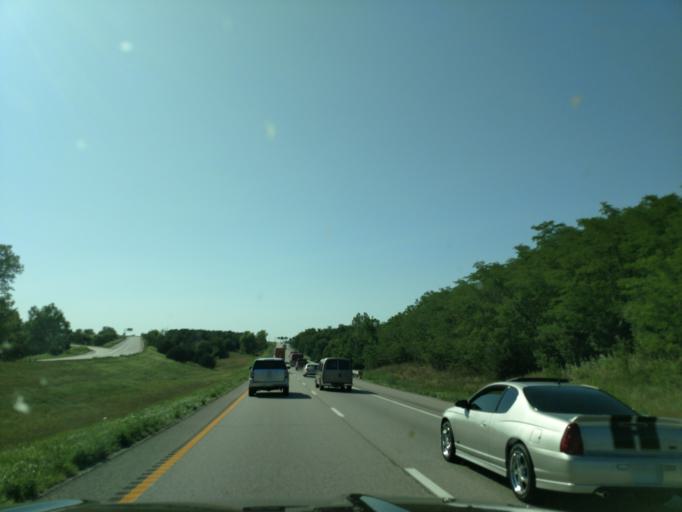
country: US
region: Missouri
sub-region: Andrew County
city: Country Club Village
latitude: 39.8813
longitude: -94.8482
